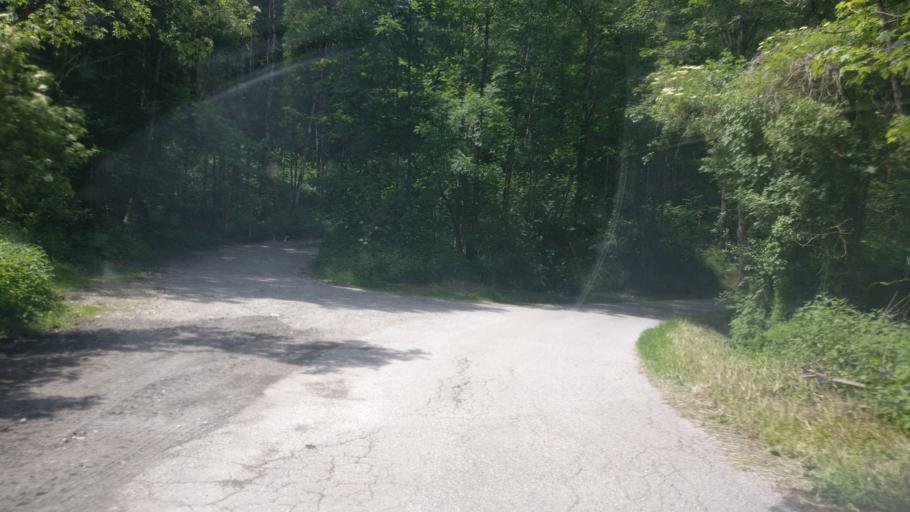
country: AT
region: Salzburg
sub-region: Politischer Bezirk Hallein
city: Kuchl
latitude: 47.6410
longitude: 13.1239
